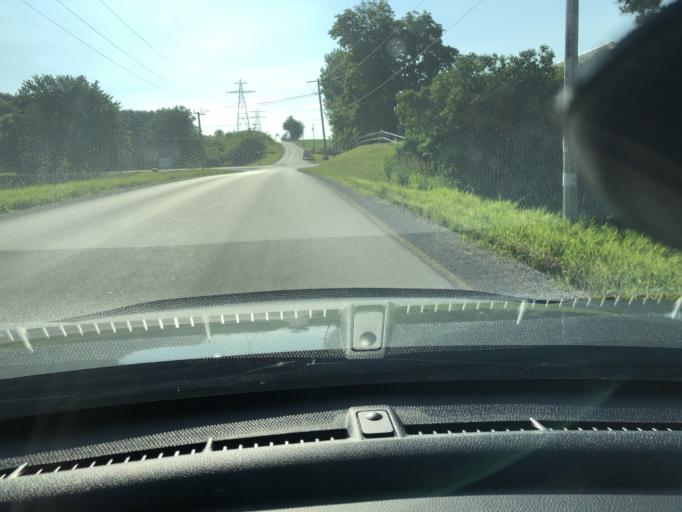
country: CA
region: Ontario
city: Stratford
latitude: 43.3878
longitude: -80.8386
